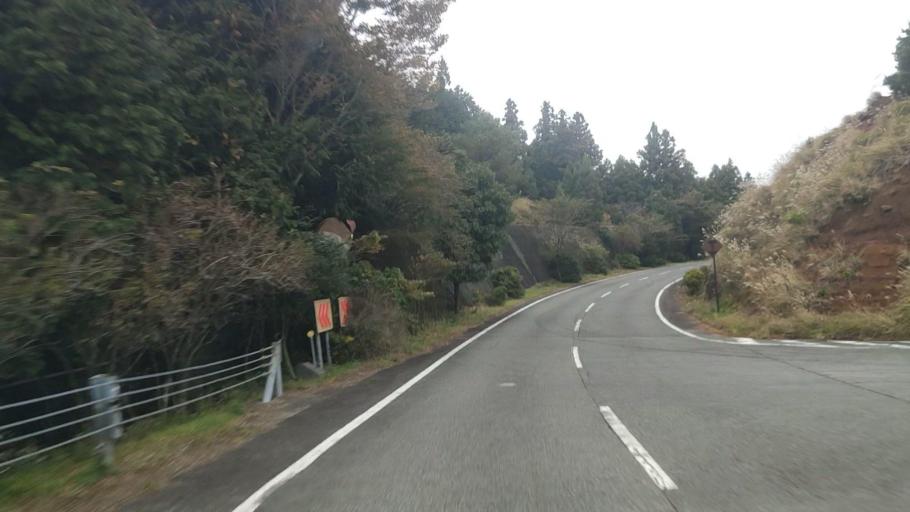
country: JP
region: Shizuoka
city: Heda
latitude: 34.8940
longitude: 138.8434
